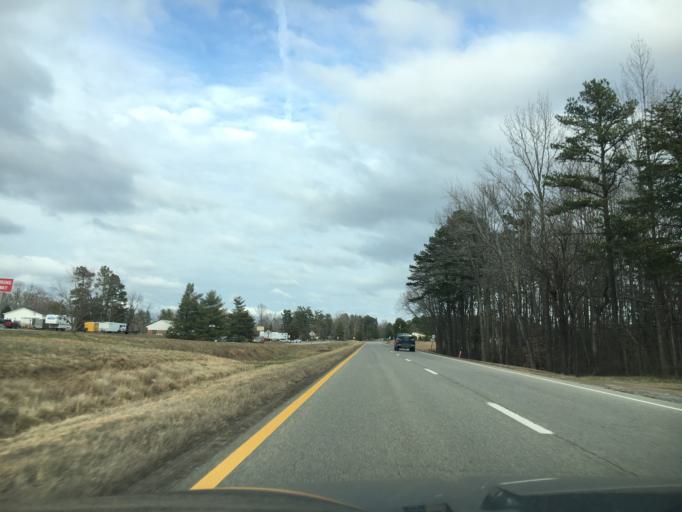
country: US
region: Virginia
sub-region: Prince Edward County
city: Hampden Sydney
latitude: 37.0770
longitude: -78.4502
